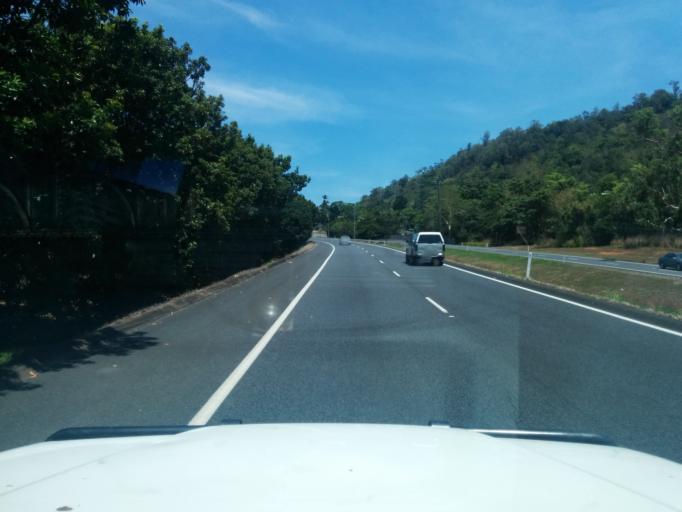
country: AU
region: Queensland
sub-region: Cairns
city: Redlynch
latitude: -16.9075
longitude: 145.7119
